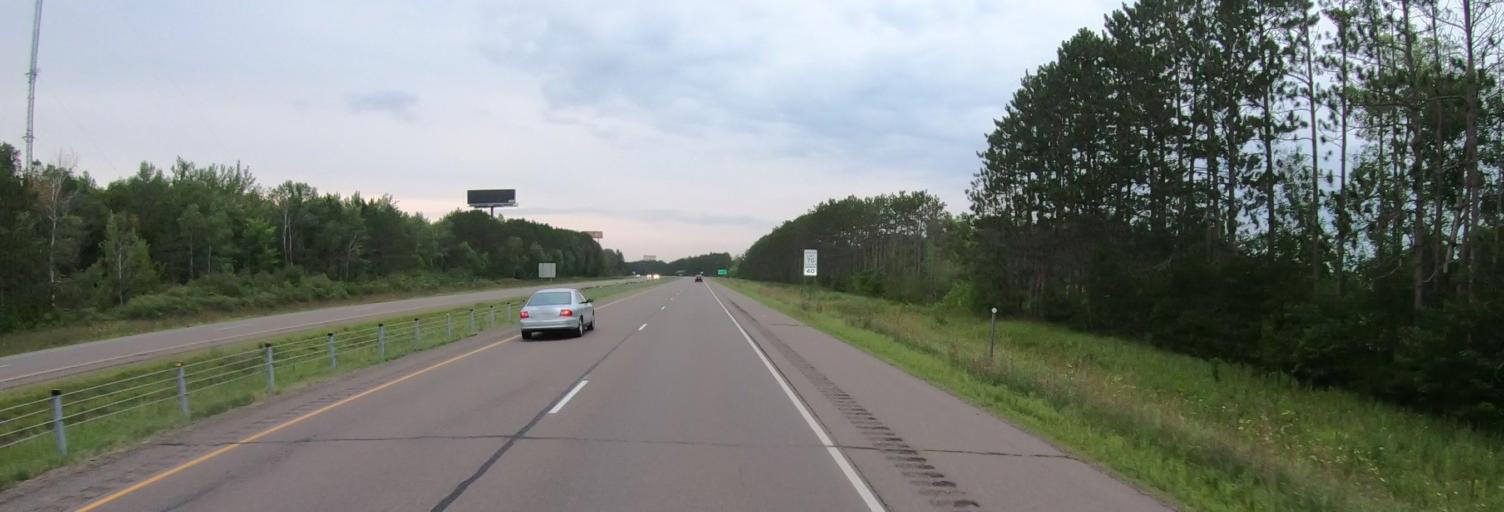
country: US
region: Minnesota
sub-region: Pine County
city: Hinckley
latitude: 46.0199
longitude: -92.9274
